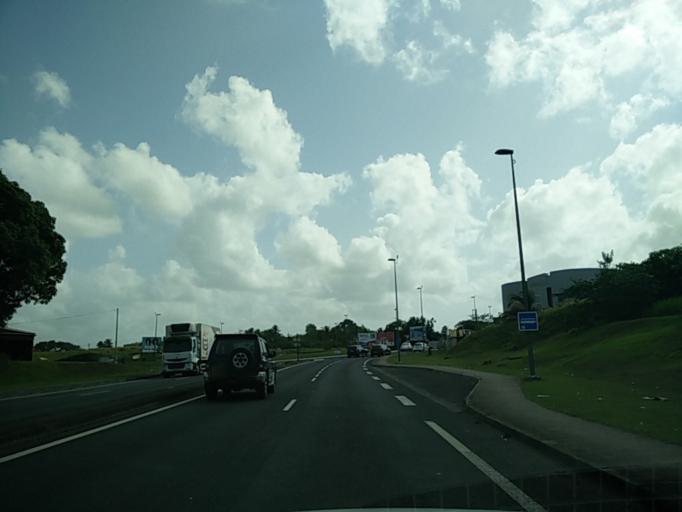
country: GP
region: Guadeloupe
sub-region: Guadeloupe
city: Les Abymes
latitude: 16.2581
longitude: -61.5116
